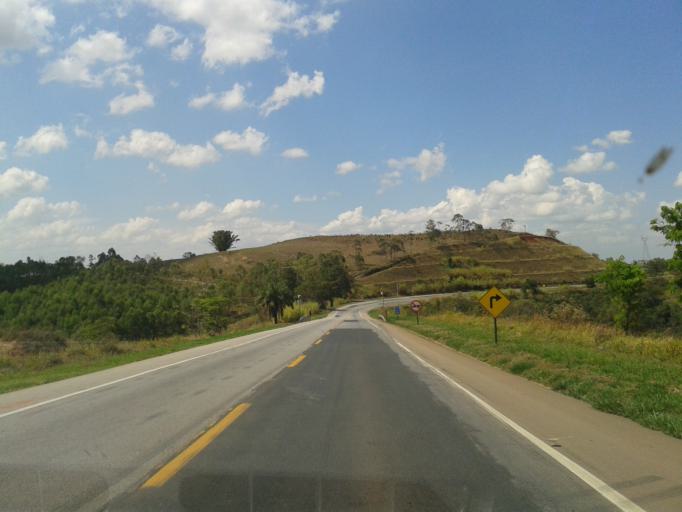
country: BR
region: Minas Gerais
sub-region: Campos Altos
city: Campos Altos
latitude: -19.7435
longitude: -45.9465
